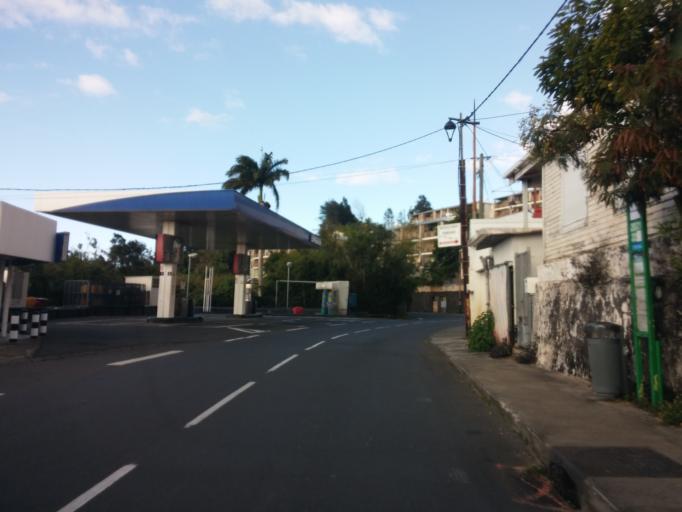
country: RE
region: Reunion
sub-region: Reunion
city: Saint-Denis
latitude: -20.8911
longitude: 55.4213
